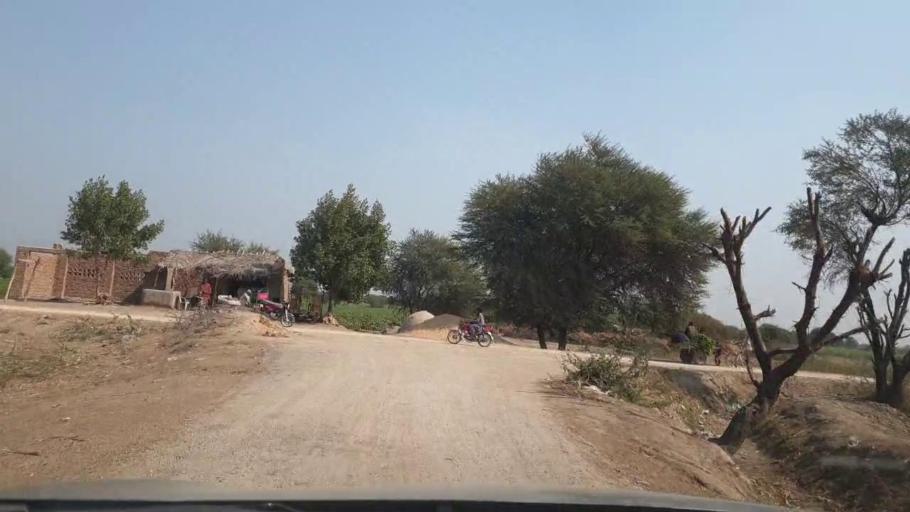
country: PK
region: Sindh
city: Tando Allahyar
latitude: 25.5570
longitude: 68.8499
